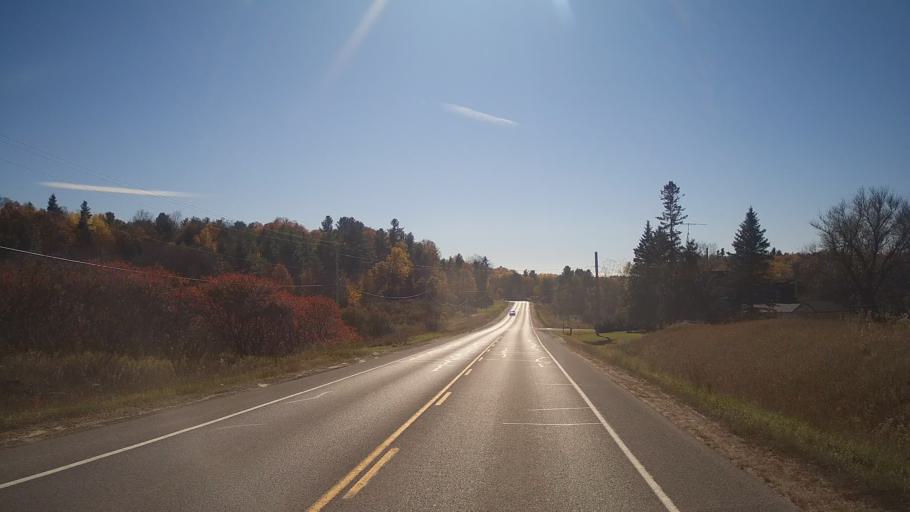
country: CA
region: Ontario
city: Kingston
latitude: 44.5530
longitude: -76.6752
